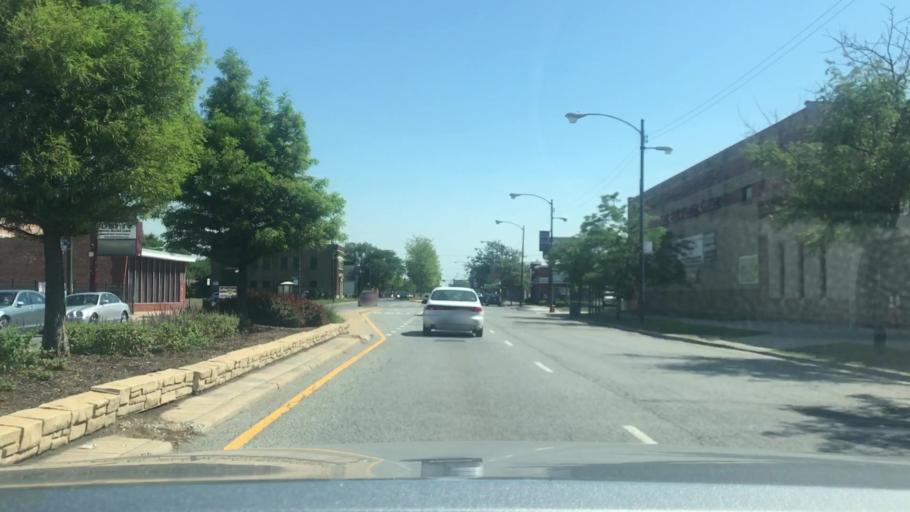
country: US
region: Illinois
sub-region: Cook County
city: Calumet Park
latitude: 41.7094
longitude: -87.6430
